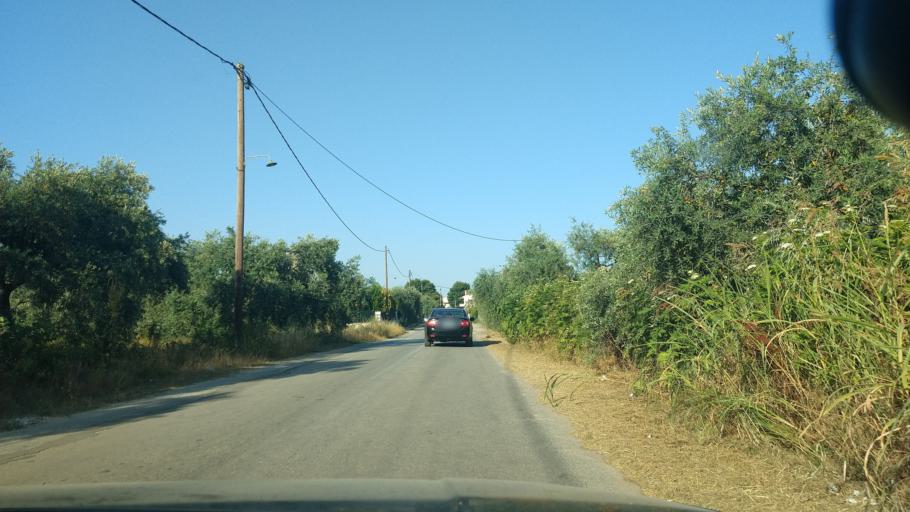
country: GR
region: East Macedonia and Thrace
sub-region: Nomos Kavalas
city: Potamia
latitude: 40.7186
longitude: 24.7508
